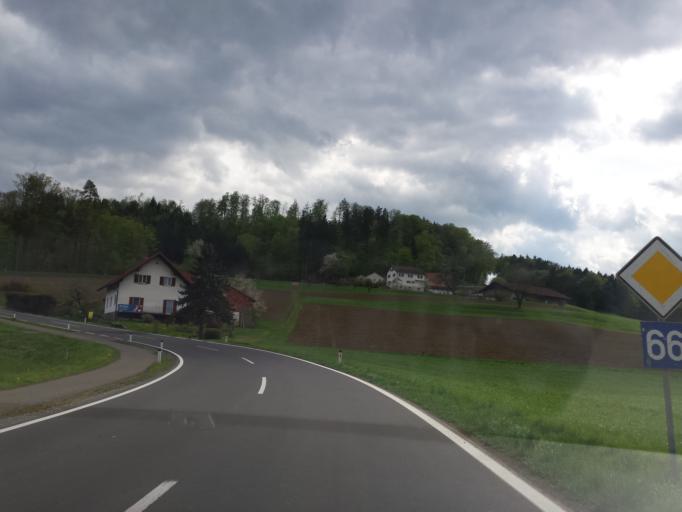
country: AT
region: Styria
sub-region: Politischer Bezirk Suedoststeiermark
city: Riegersburg
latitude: 46.9970
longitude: 15.9307
